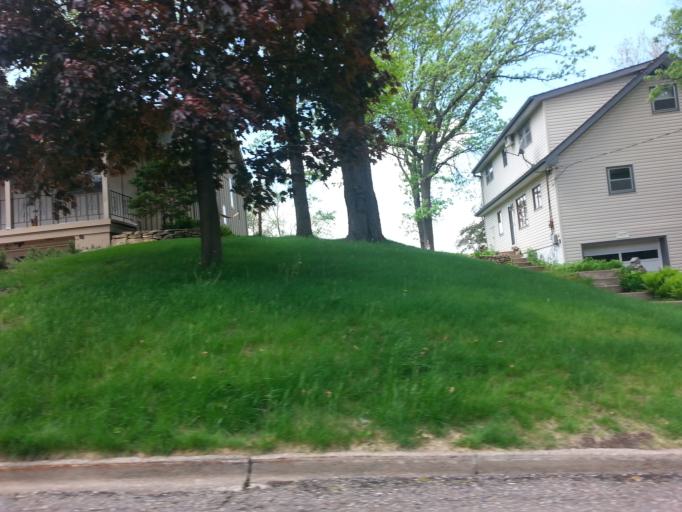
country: US
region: Wisconsin
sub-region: Saint Croix County
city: Hudson
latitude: 44.9801
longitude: -92.7426
